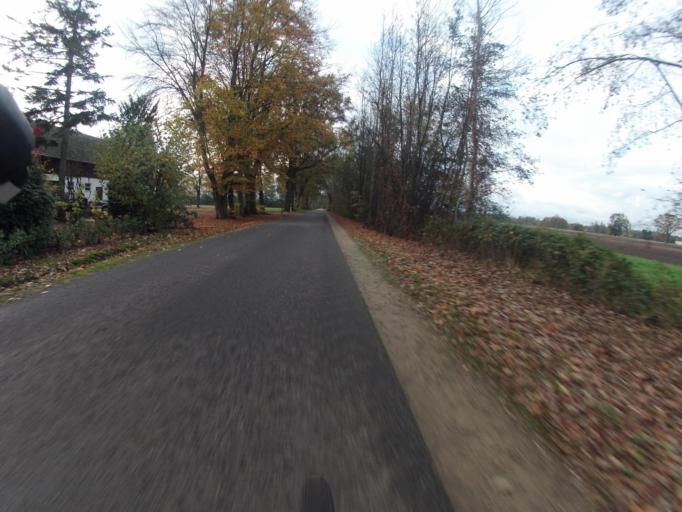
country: DE
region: North Rhine-Westphalia
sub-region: Regierungsbezirk Munster
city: Horstel
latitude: 52.2616
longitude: 7.5662
